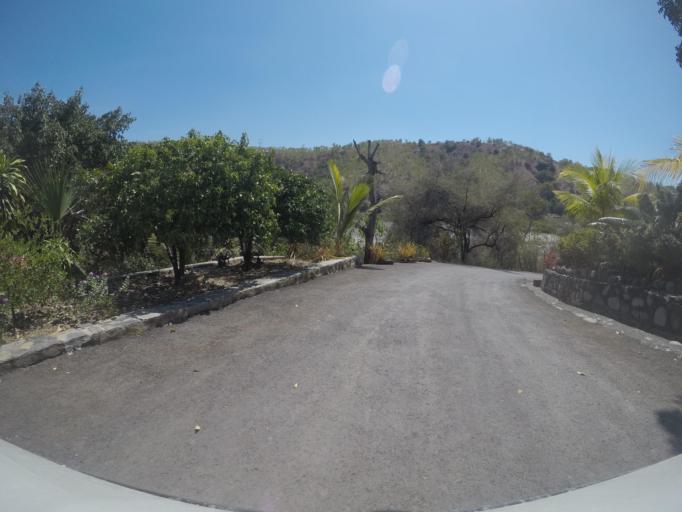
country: TL
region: Dili
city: Dili
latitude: -8.5761
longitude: 125.4740
